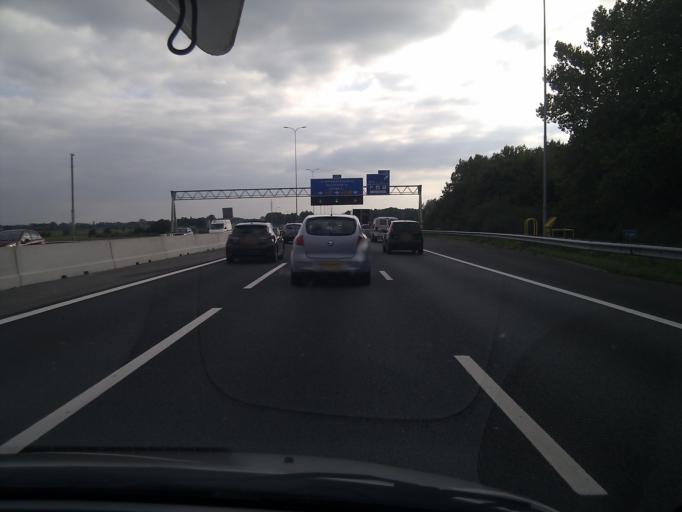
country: NL
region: Utrecht
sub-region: Gemeente Utrecht
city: Lunetten
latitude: 52.0234
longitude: 5.1288
